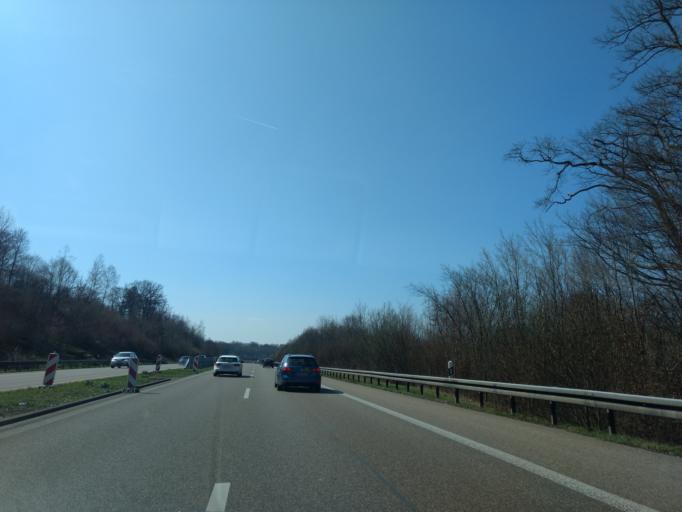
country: DE
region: Baden-Wuerttemberg
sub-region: Regierungsbezirk Stuttgart
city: Reichenbach an der Fils
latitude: 48.7100
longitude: 9.4882
